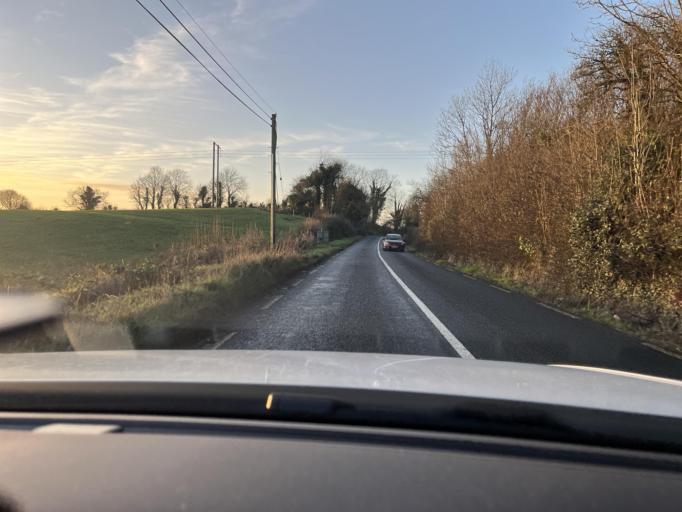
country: IE
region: Ulster
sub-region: An Cabhan
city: Ballyconnell
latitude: 54.0917
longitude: -7.6301
